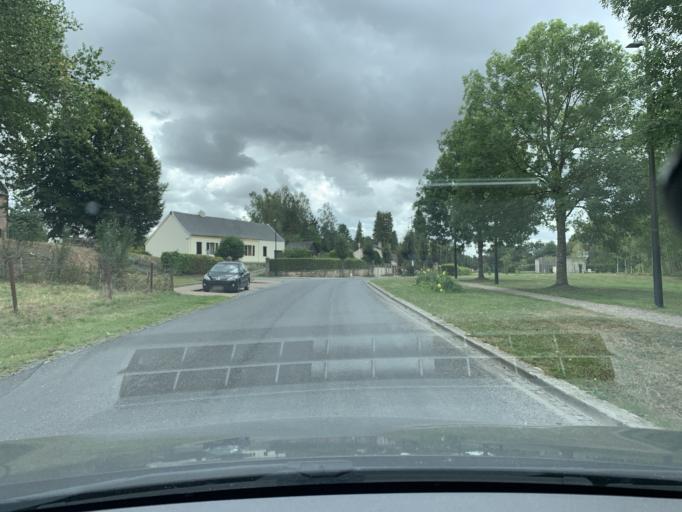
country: FR
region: Picardie
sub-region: Departement de l'Aisne
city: Saint-Michel
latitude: 49.9263
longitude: 4.1349
